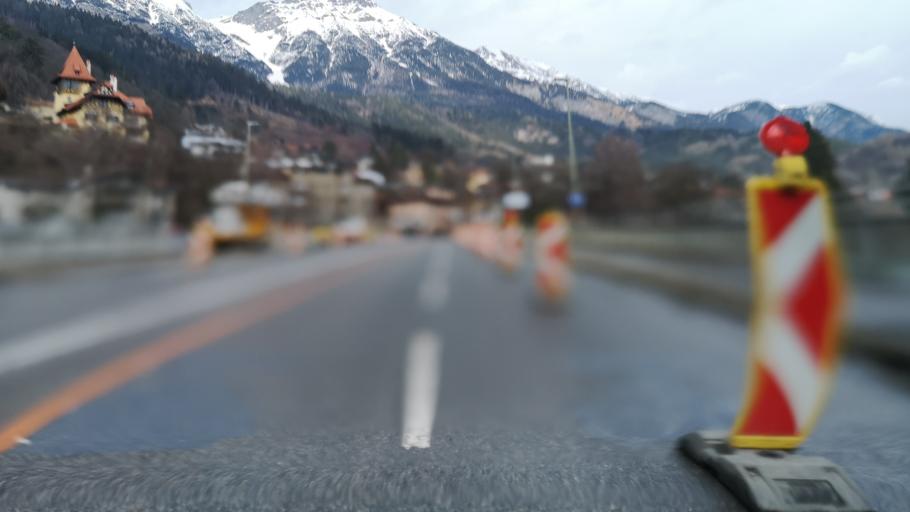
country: AT
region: Tyrol
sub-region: Innsbruck Stadt
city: Innsbruck
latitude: 47.2798
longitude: 11.4048
